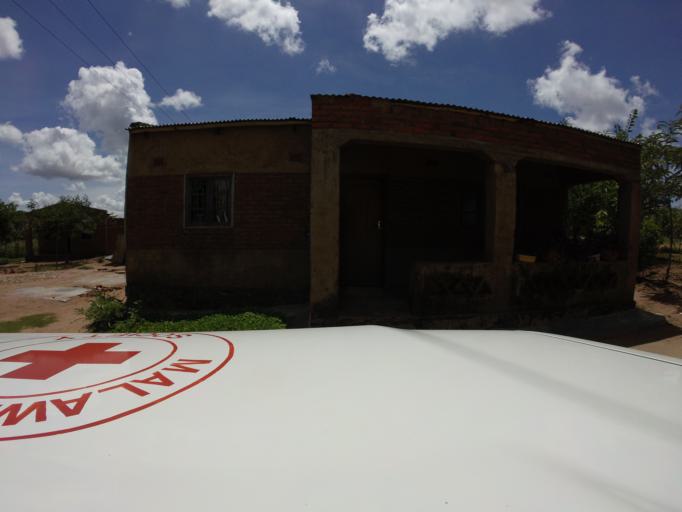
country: MW
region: Southern Region
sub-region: Thyolo District
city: Thyolo
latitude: -15.9538
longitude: 35.1579
